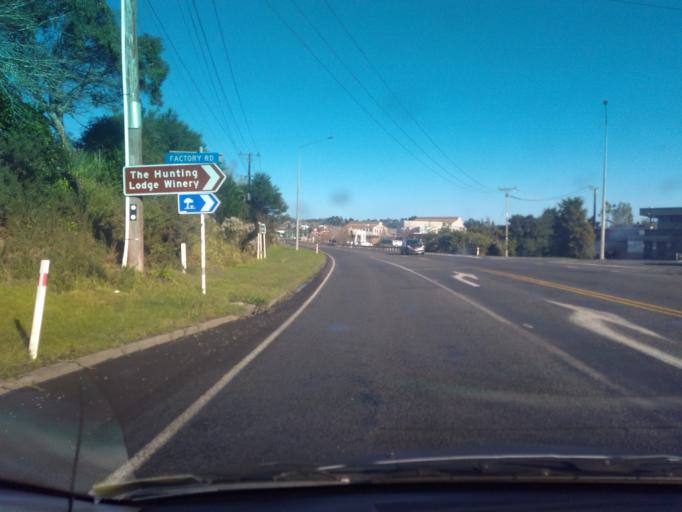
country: NZ
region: Auckland
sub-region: Auckland
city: Muriwai Beach
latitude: -36.7669
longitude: 174.4964
